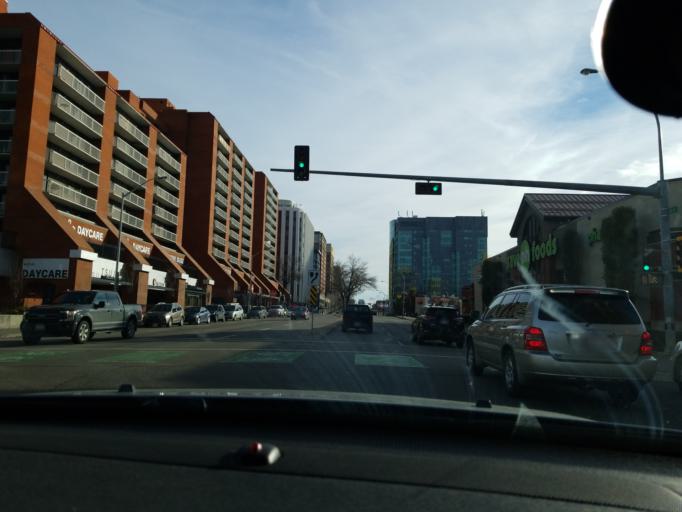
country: CA
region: Alberta
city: Edmonton
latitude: 53.5437
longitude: -113.5085
